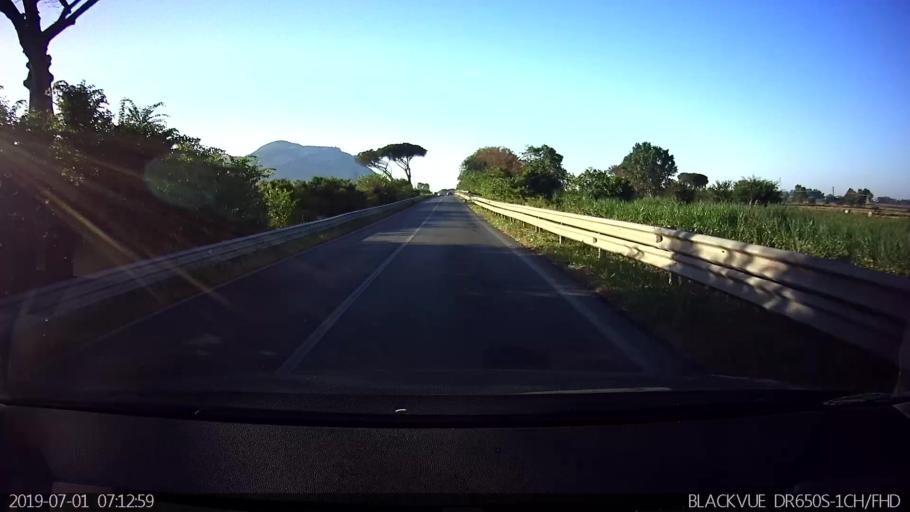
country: IT
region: Latium
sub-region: Provincia di Latina
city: Borgo Hermada
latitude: 41.3306
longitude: 13.1724
